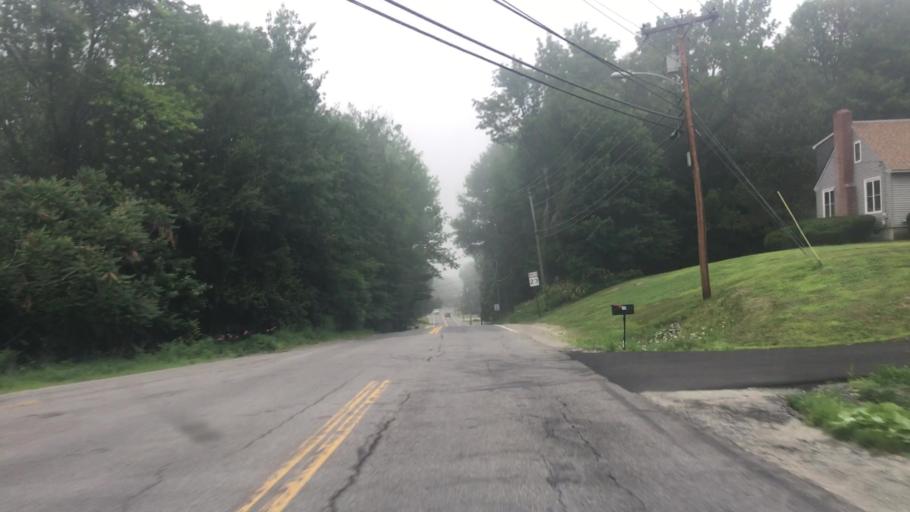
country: US
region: Maine
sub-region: Kennebec County
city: Oakland
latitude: 44.5319
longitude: -69.7239
